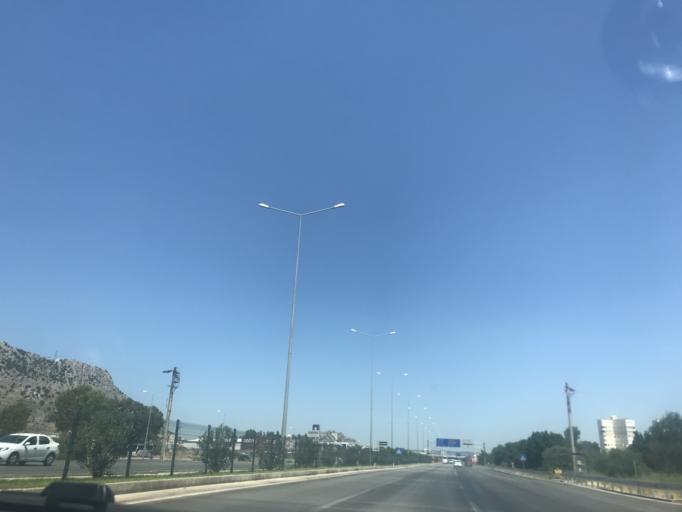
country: TR
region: Antalya
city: Cakirlar
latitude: 36.8399
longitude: 30.5966
